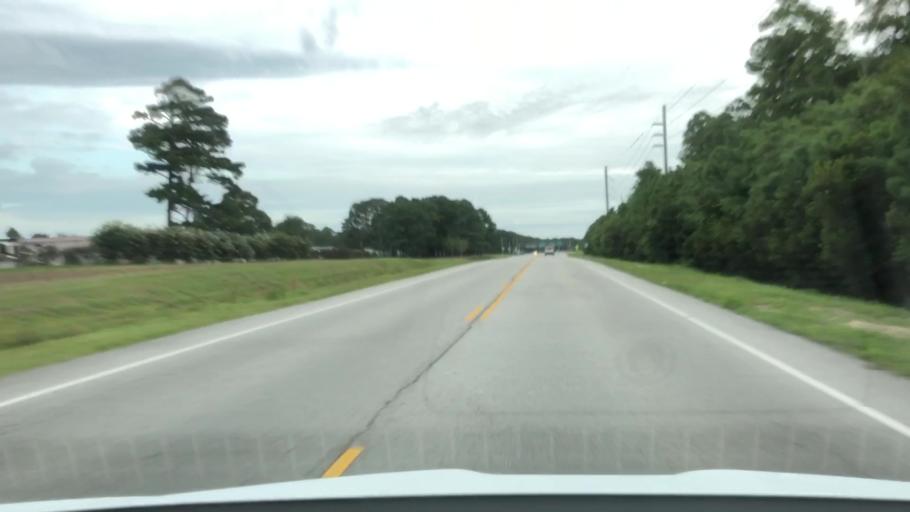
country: US
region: North Carolina
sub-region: Carteret County
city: Cedar Point
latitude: 34.6824
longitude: -77.0679
